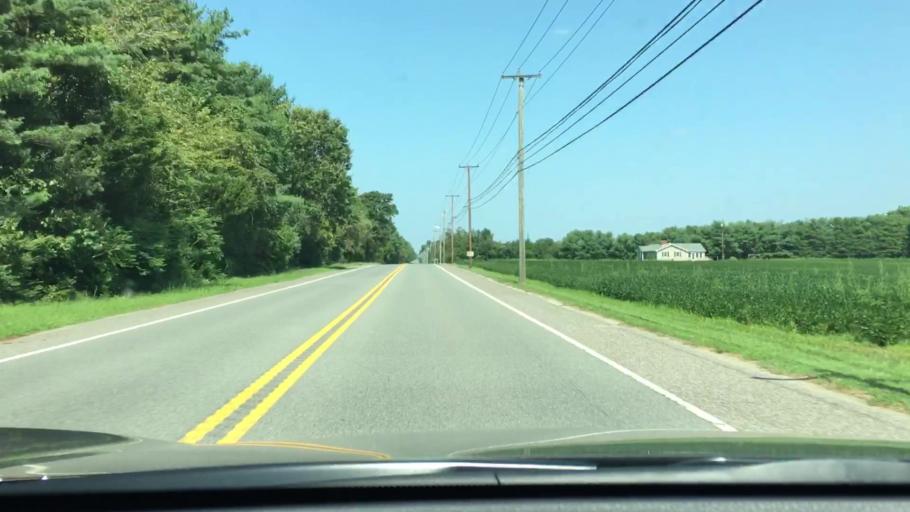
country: US
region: New Jersey
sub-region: Cumberland County
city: Laurel Lake
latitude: 39.2951
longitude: -74.9985
